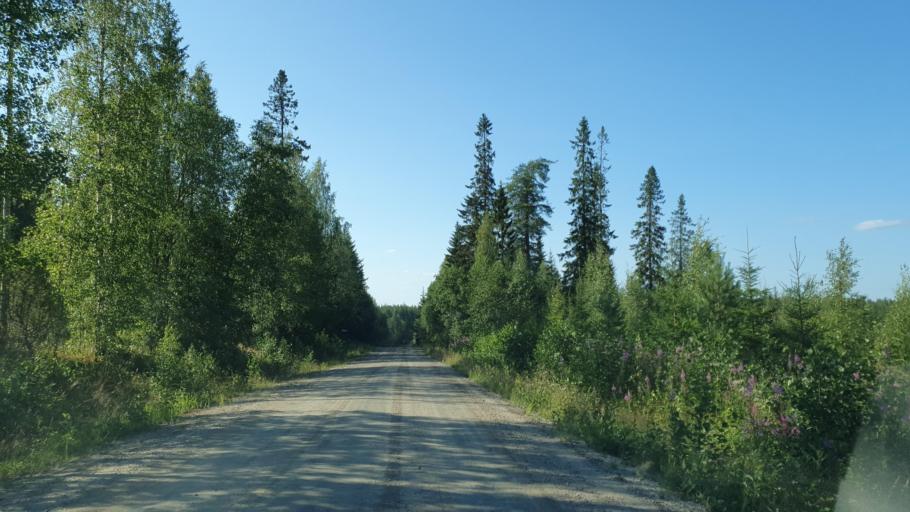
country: FI
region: Kainuu
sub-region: Kehys-Kainuu
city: Kuhmo
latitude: 64.0336
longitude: 29.6812
